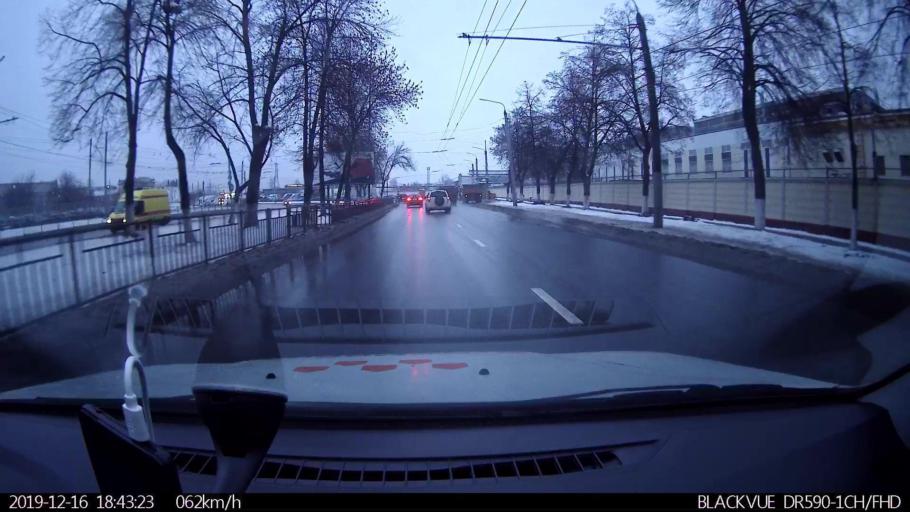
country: RU
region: Nizjnij Novgorod
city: Nizhniy Novgorod
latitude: 56.2567
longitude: 43.9017
